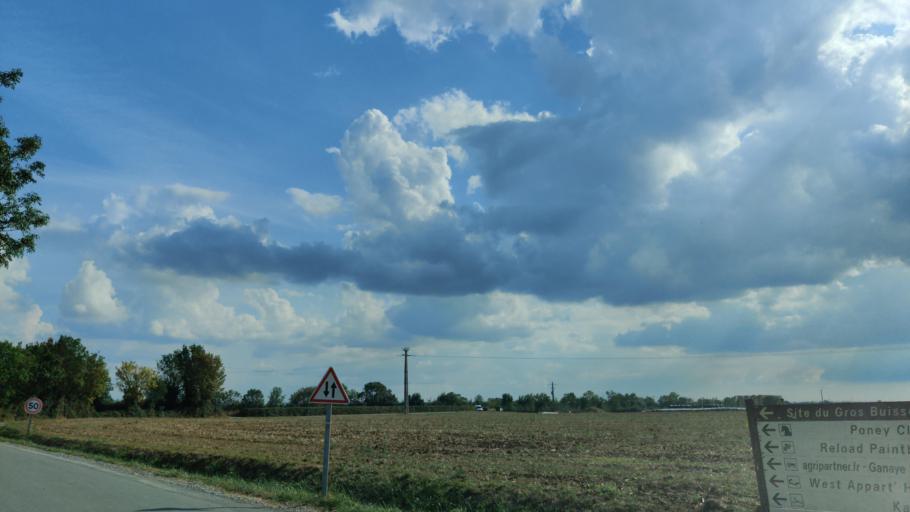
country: FR
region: Poitou-Charentes
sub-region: Departement des Deux-Sevres
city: Bessines
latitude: 46.2969
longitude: -0.5131
